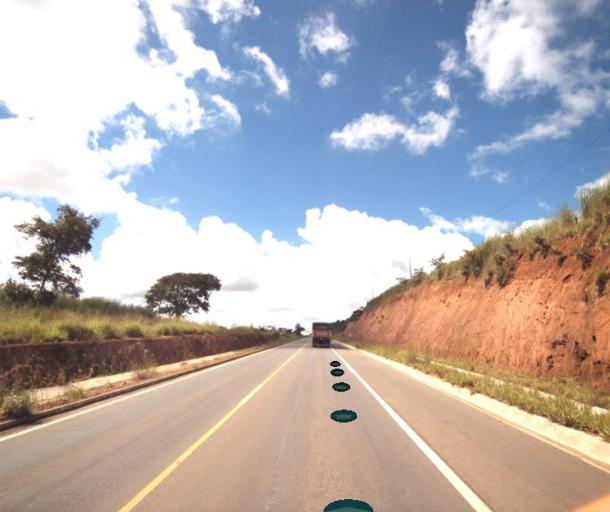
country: BR
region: Goias
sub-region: Anapolis
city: Anapolis
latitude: -16.1832
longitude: -49.0406
